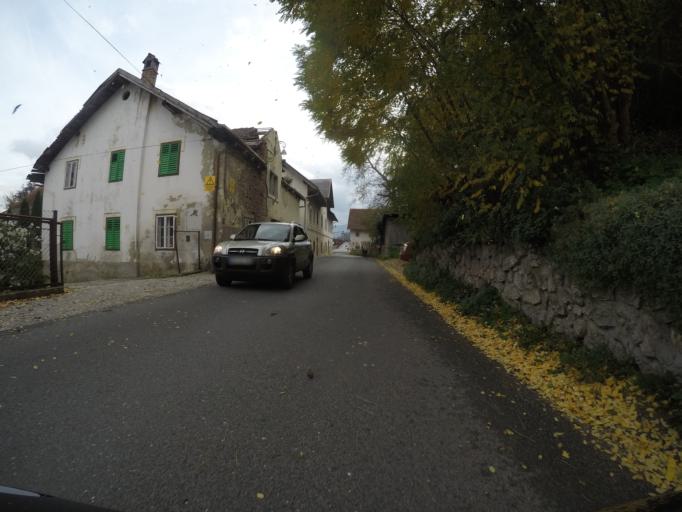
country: SI
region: Bled
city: Bled
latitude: 46.3735
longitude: 14.1039
